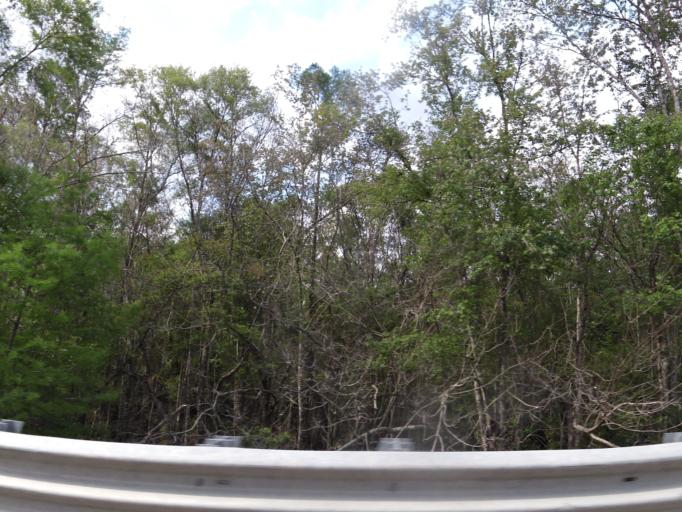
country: US
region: Georgia
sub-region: Charlton County
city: Folkston
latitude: 30.8225
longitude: -82.0551
